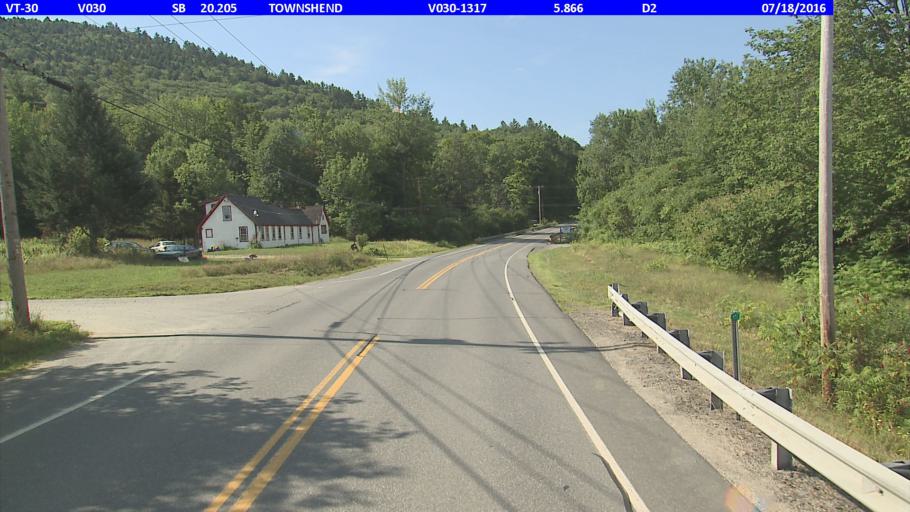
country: US
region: Vermont
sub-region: Windham County
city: Newfane
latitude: 43.0767
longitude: -72.7041
